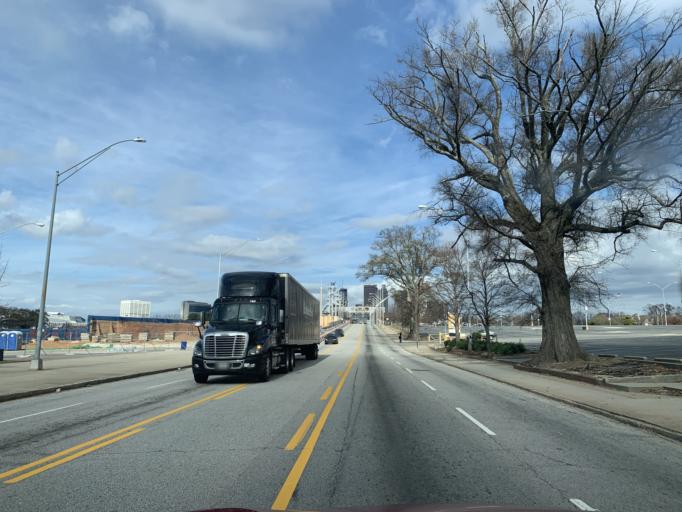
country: US
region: Georgia
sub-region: Fulton County
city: Atlanta
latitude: 33.7374
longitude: -84.3878
